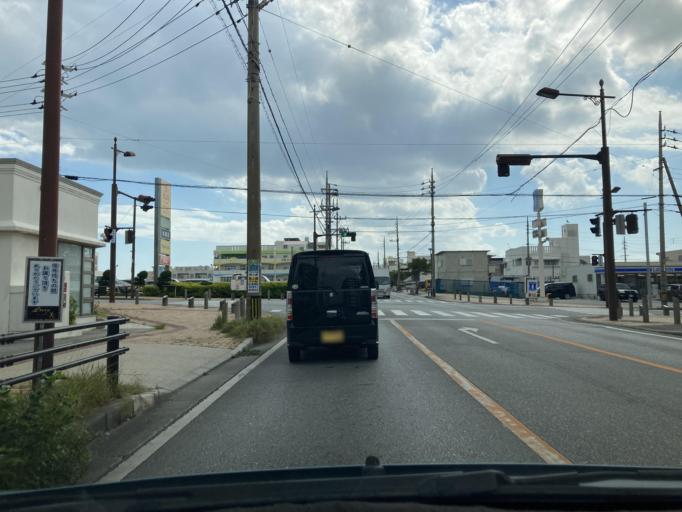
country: JP
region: Okinawa
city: Ginowan
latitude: 26.2504
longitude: 127.7740
